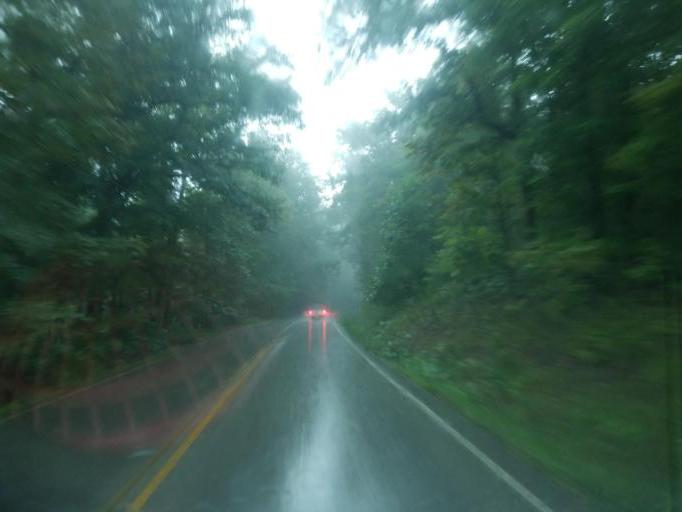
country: US
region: Kentucky
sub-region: Carter County
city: Olive Hill
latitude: 38.3462
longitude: -83.2019
